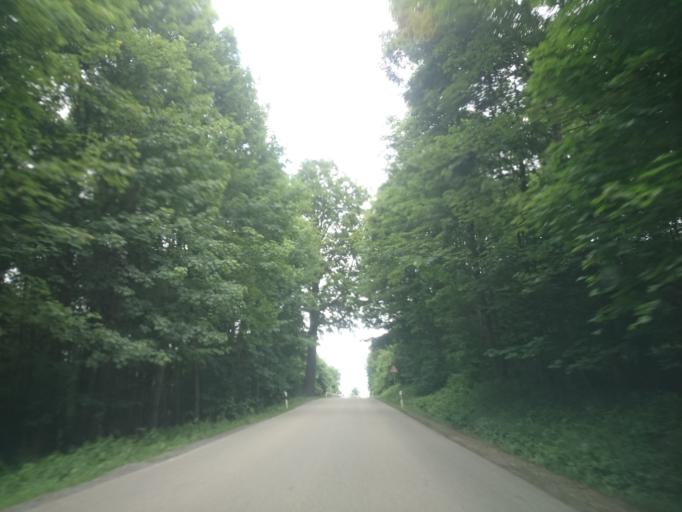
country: DE
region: Saxony
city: Eppendorf
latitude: 50.7777
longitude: 13.2096
